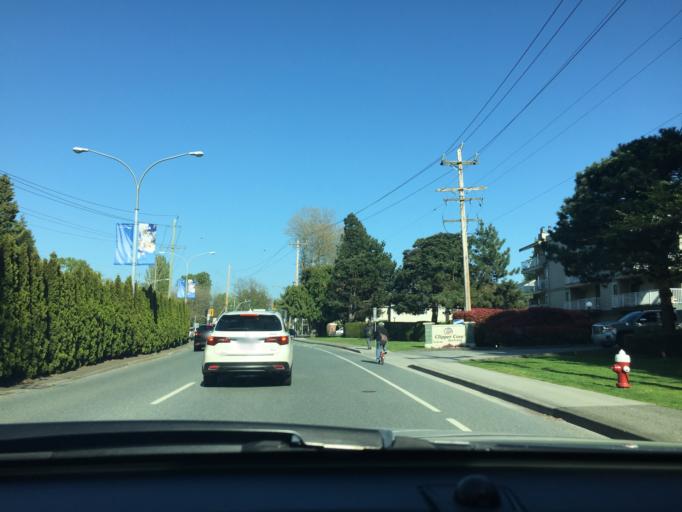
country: CA
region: British Columbia
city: Richmond
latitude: 49.1627
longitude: -123.1275
